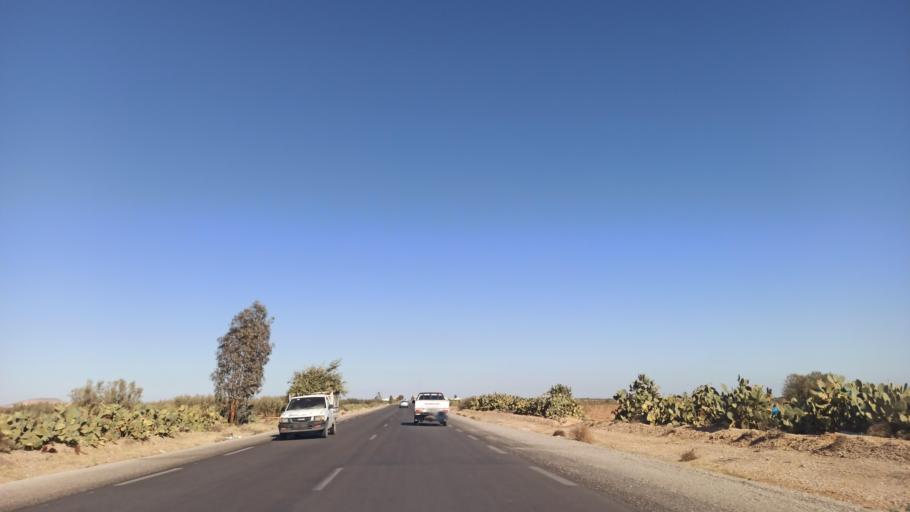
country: TN
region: Sidi Bu Zayd
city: Bi'r al Hufayy
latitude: 34.9610
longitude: 9.2210
